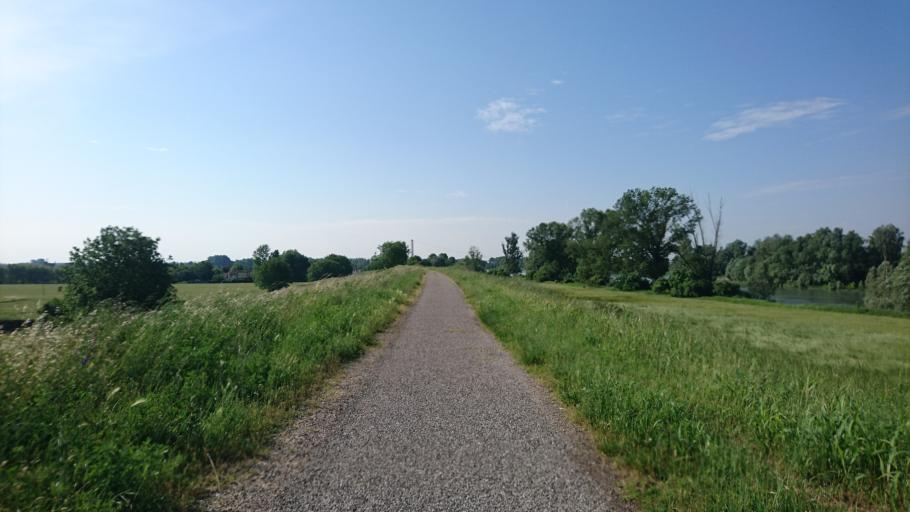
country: IT
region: Veneto
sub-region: Provincia di Verona
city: Villa Bartolomea
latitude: 45.1856
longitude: 11.3258
